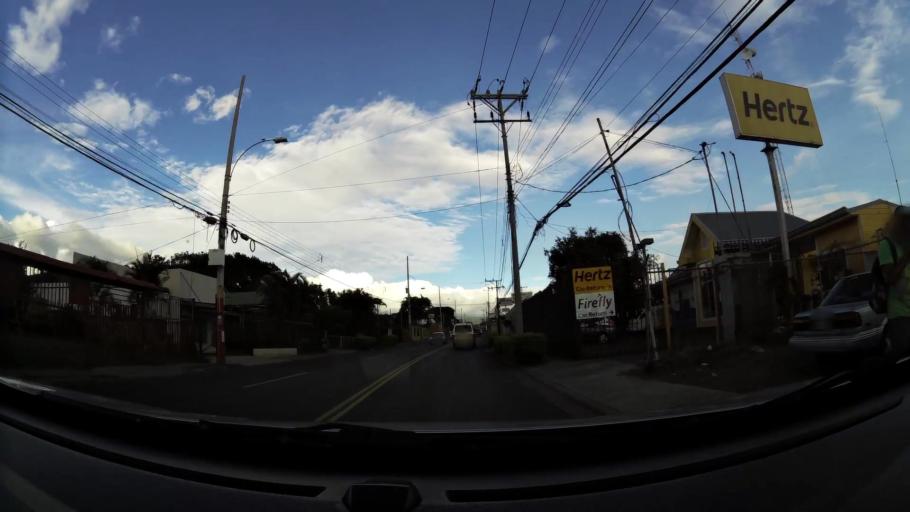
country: CR
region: Heredia
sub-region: Canton de Belen
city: San Antonio
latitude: 10.0016
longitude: -84.1913
